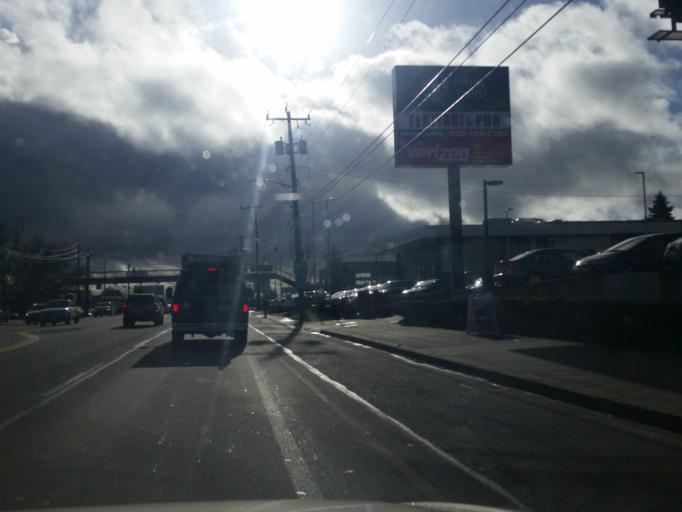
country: US
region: Washington
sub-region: King County
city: Shoreline
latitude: 47.7245
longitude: -122.3451
